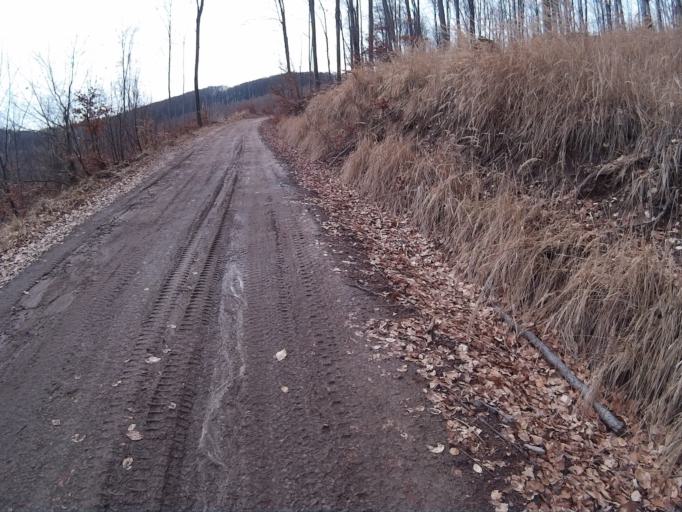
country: HU
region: Borsod-Abauj-Zemplen
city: Tolcsva
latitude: 48.4037
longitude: 21.4209
